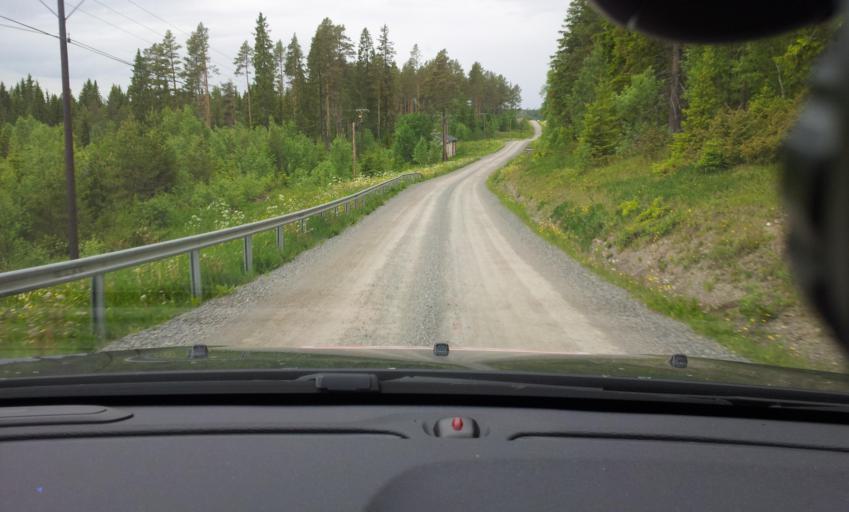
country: SE
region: Jaemtland
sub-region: OEstersunds Kommun
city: Brunflo
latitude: 62.9663
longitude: 14.6995
